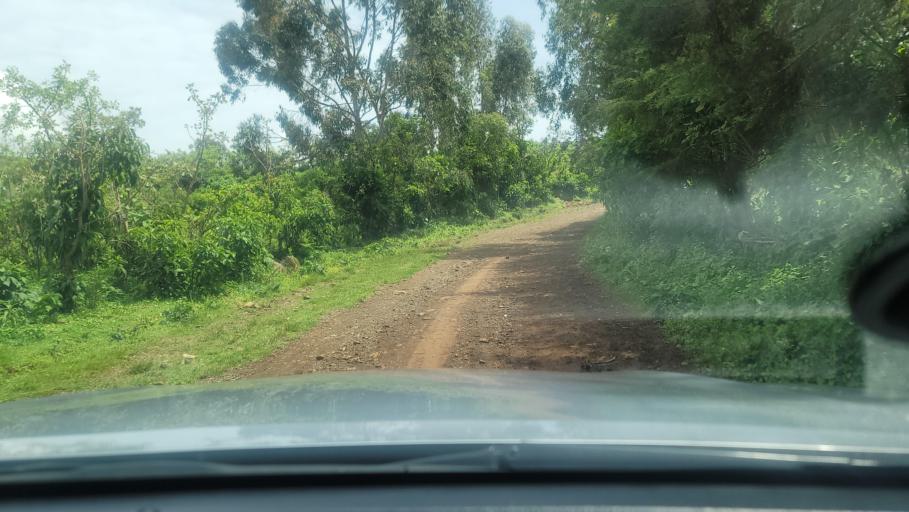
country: ET
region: Oromiya
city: Agaro
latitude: 7.8339
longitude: 36.4052
